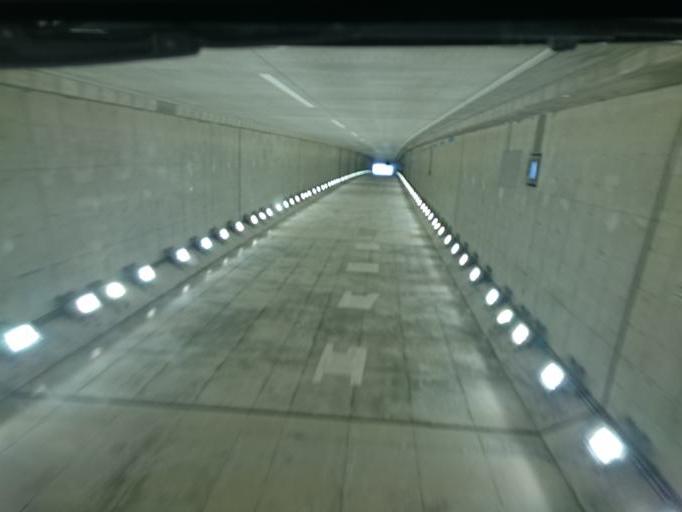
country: JP
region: Mie
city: Komono
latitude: 34.9931
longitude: 136.5538
